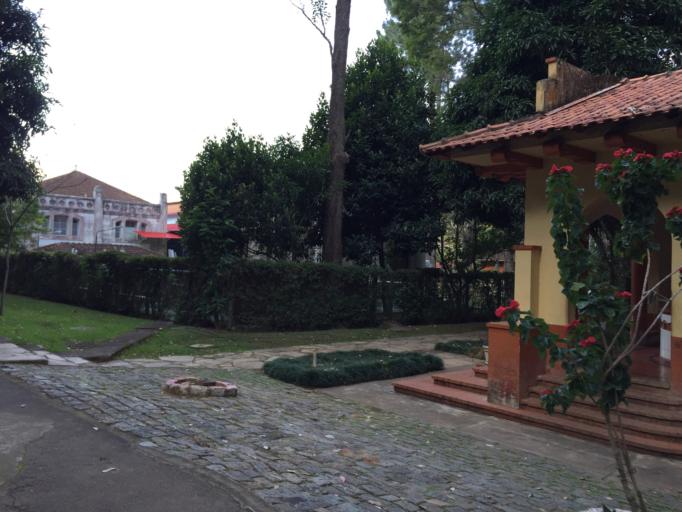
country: BR
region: Minas Gerais
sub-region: Caxambu
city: Caxambu
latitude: -21.9823
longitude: -44.9376
